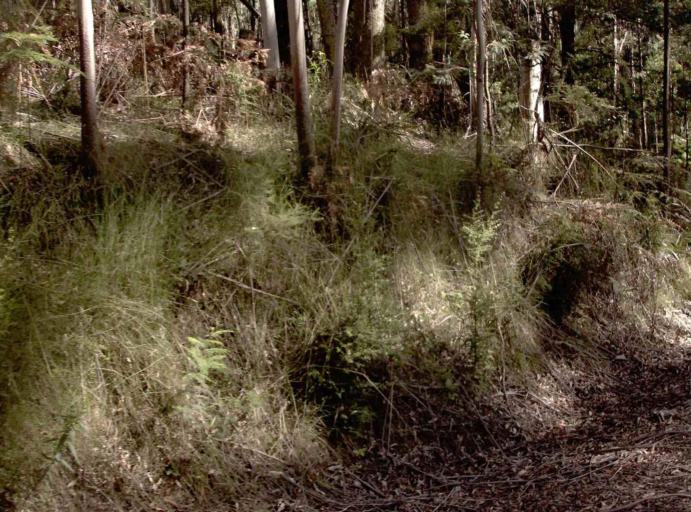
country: AU
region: Victoria
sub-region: East Gippsland
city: Lakes Entrance
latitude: -37.3966
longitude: 148.5932
